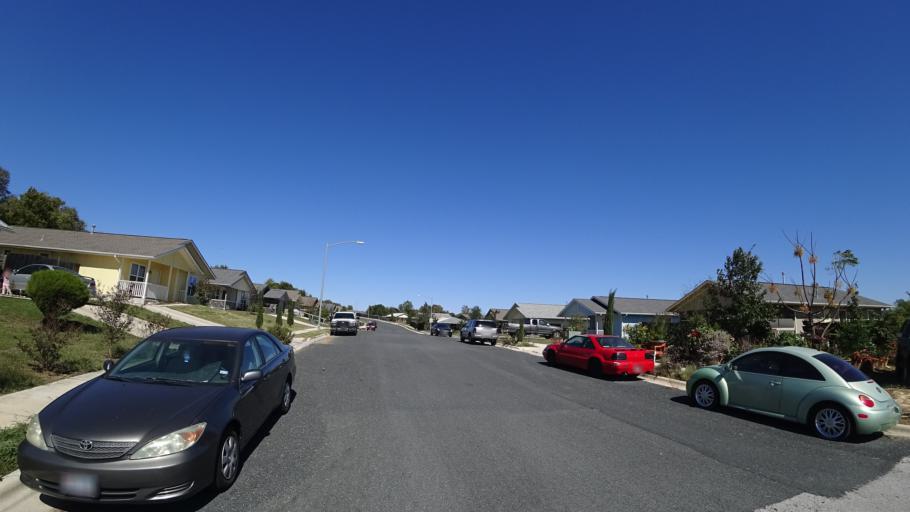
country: US
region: Texas
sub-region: Travis County
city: Hornsby Bend
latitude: 30.2933
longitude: -97.6483
